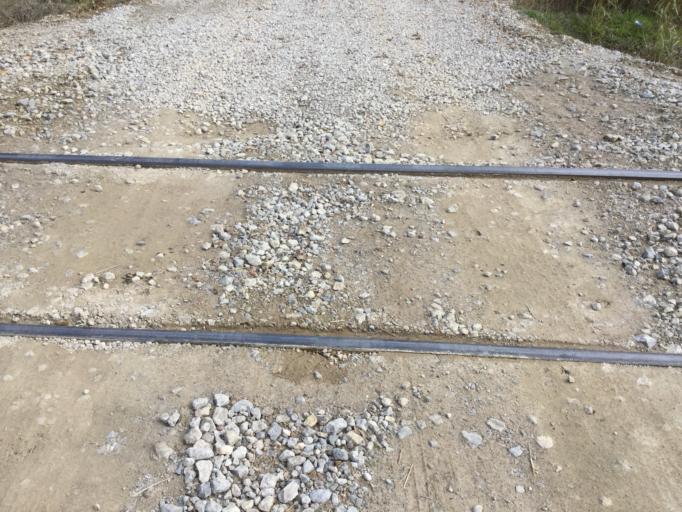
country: US
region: Kansas
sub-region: Montgomery County
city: Cherryvale
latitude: 37.2452
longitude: -95.5571
